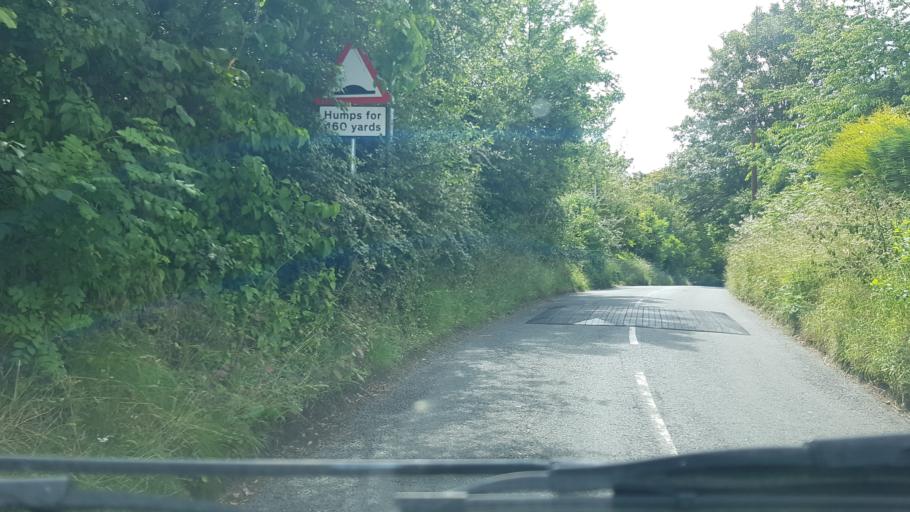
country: GB
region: England
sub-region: Worcestershire
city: Stourport-on-Severn
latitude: 52.3449
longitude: -2.2800
